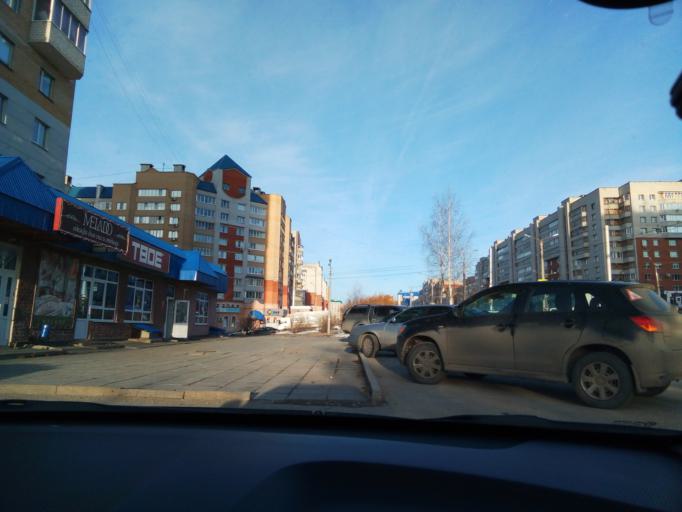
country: RU
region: Chuvashia
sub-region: Cheboksarskiy Rayon
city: Cheboksary
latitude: 56.1491
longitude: 47.1703
